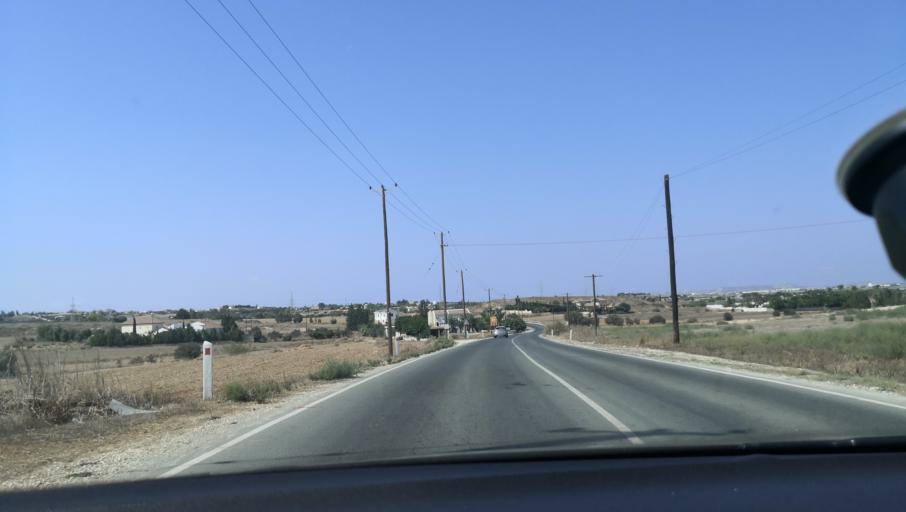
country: CY
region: Lefkosia
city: Kato Deftera
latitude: 35.1211
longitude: 33.2585
